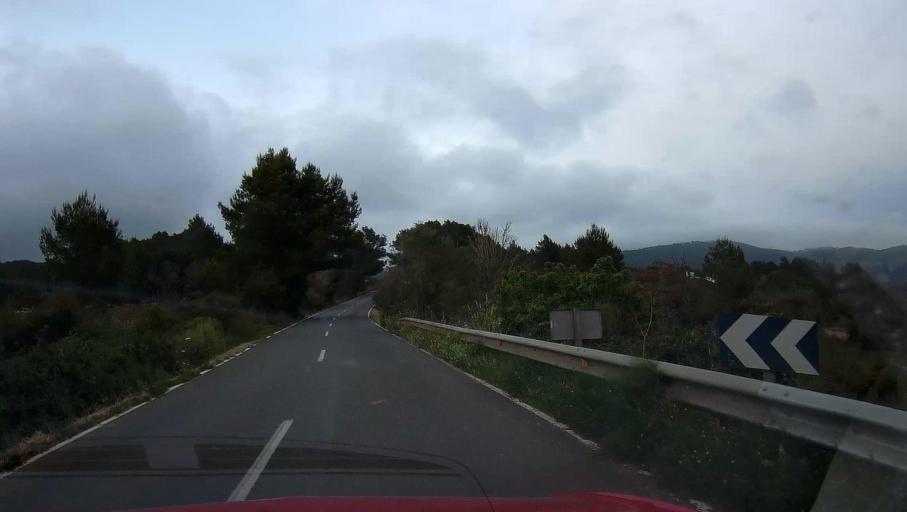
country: ES
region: Balearic Islands
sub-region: Illes Balears
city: Sant Joan de Labritja
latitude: 39.0635
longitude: 1.4802
